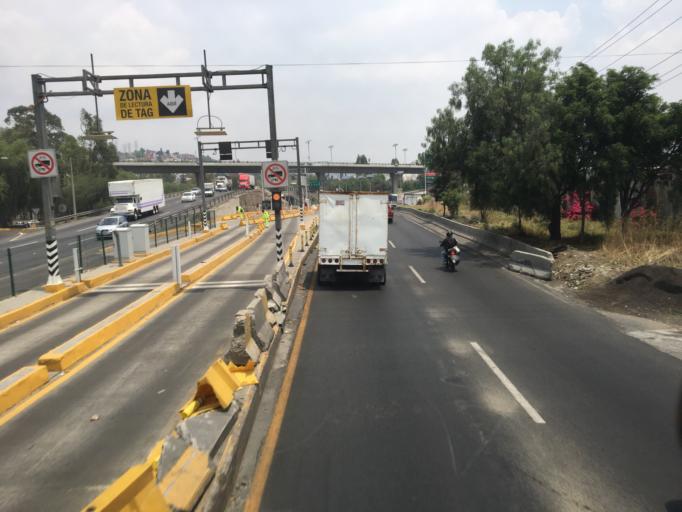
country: MX
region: Mexico
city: Tlalnepantla
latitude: 19.5679
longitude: -99.2073
